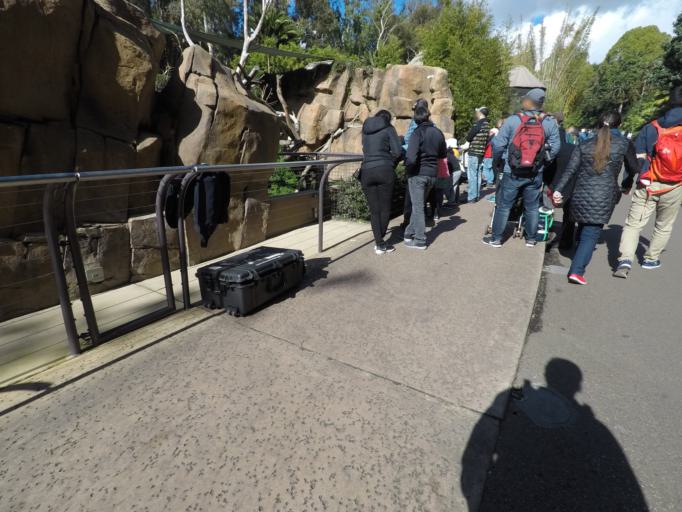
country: US
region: California
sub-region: San Diego County
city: San Diego
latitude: 32.7362
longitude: -117.1502
